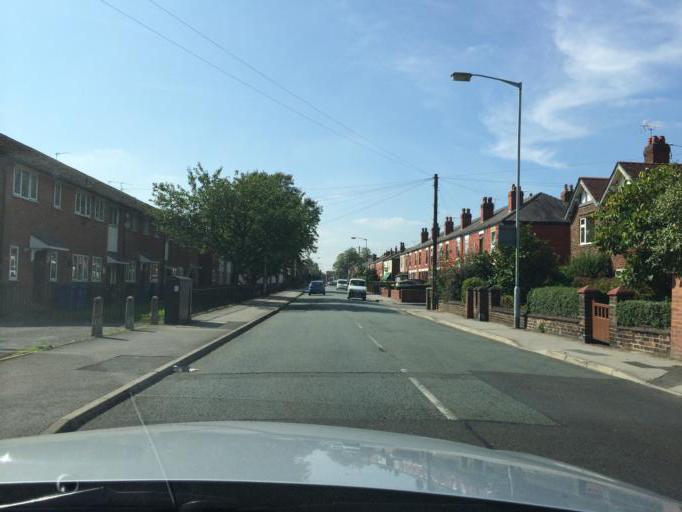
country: GB
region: England
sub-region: Borough of Stockport
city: Hazel Grove
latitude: 53.3839
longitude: -2.1187
